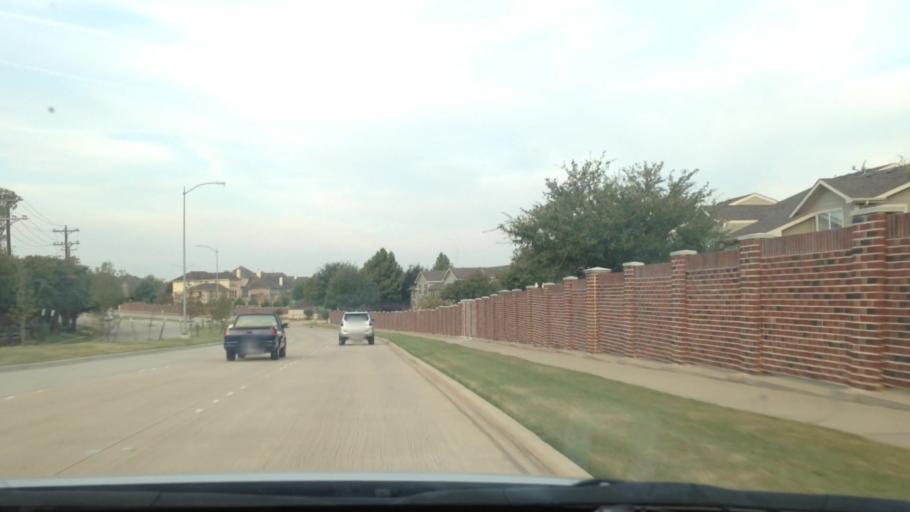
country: US
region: Texas
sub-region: Collin County
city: Frisco
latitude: 33.1122
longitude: -96.7532
